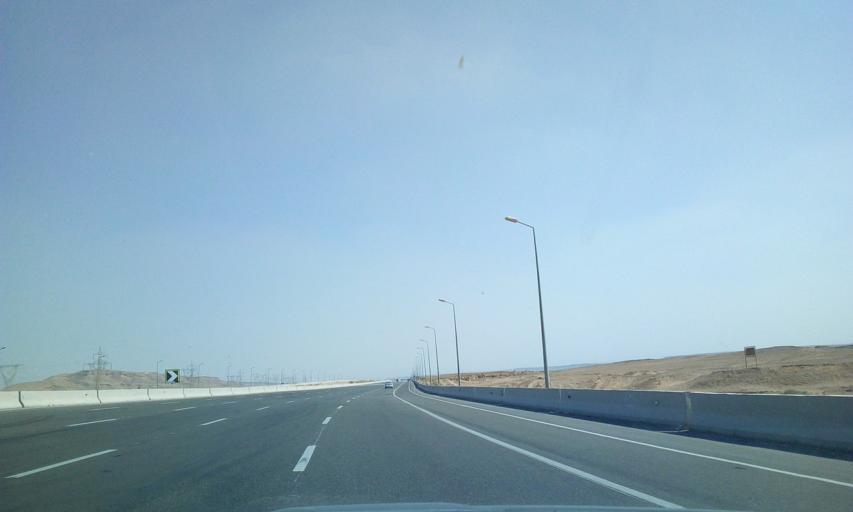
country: EG
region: As Suways
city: Ain Sukhna
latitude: 29.8599
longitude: 31.8681
